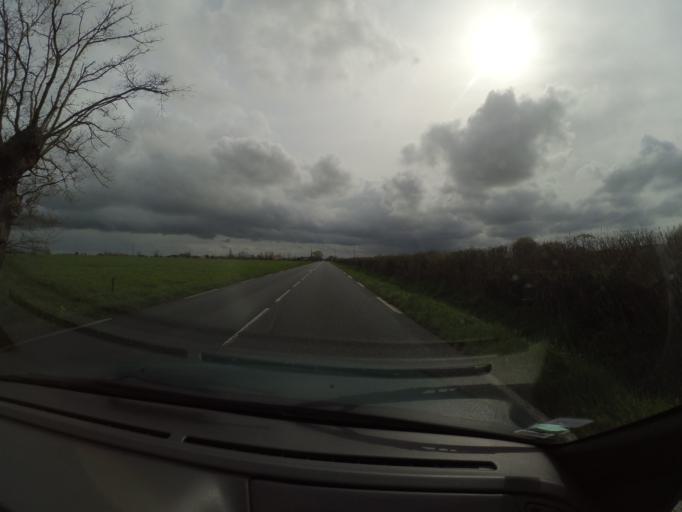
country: FR
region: Pays de la Loire
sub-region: Departement de Maine-et-Loire
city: Landemont
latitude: 47.2475
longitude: -1.2094
